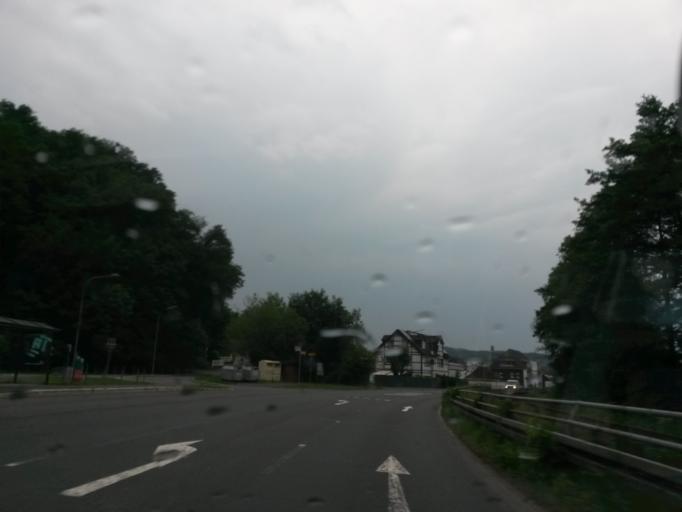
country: DE
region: North Rhine-Westphalia
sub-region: Regierungsbezirk Koln
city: Overath
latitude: 50.9537
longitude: 7.3100
